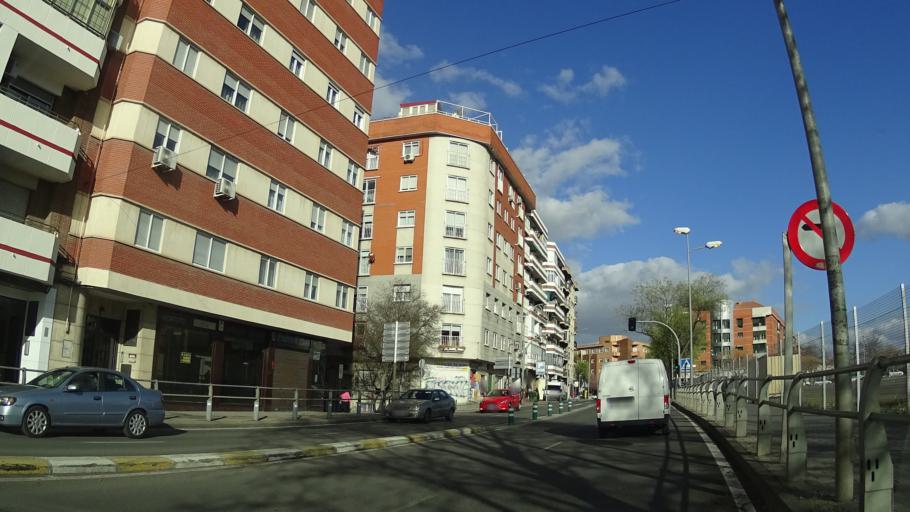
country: ES
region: Castille-La Mancha
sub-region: Provincia de Ciudad Real
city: Ciudad Real
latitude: 38.9799
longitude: -3.9288
